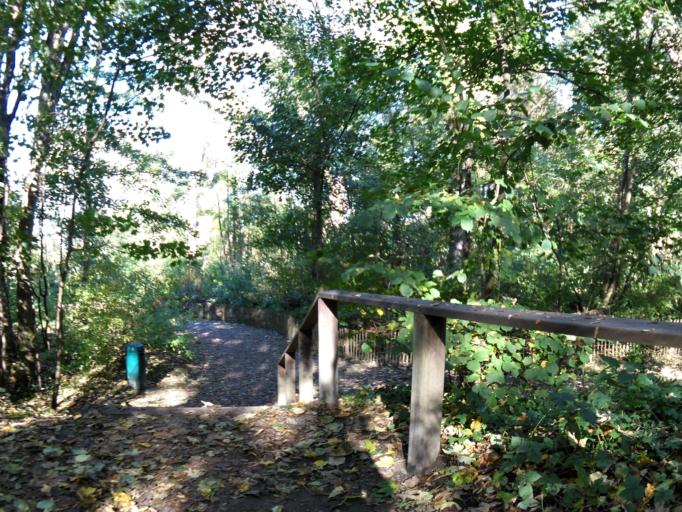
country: BE
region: Flanders
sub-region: Provincie Vlaams-Brabant
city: Dilbeek
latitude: 50.8594
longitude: 4.2910
